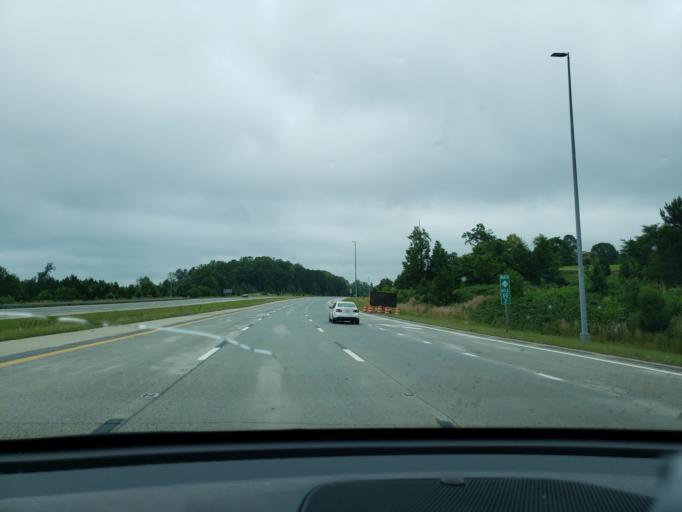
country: US
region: North Carolina
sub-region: Wake County
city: Green Level
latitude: 35.7564
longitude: -78.8916
